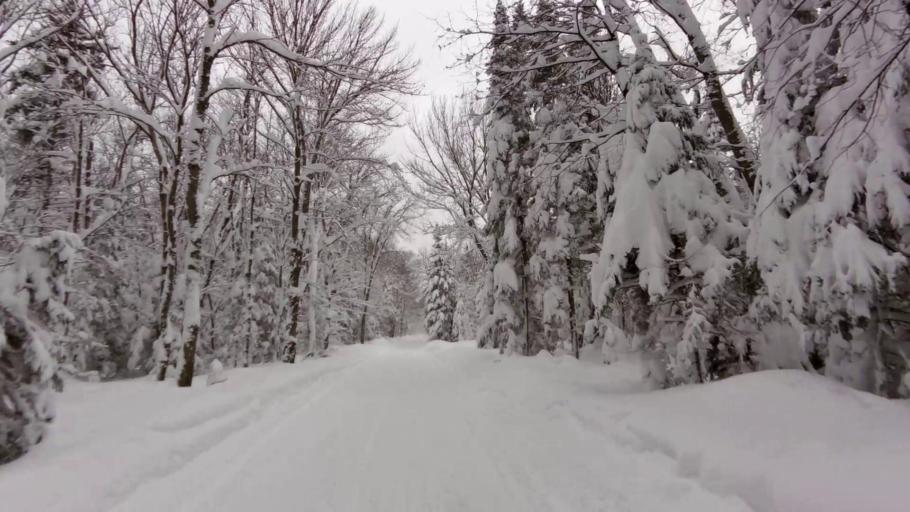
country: US
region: New York
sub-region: Lewis County
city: Lowville
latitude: 43.7315
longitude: -75.6373
